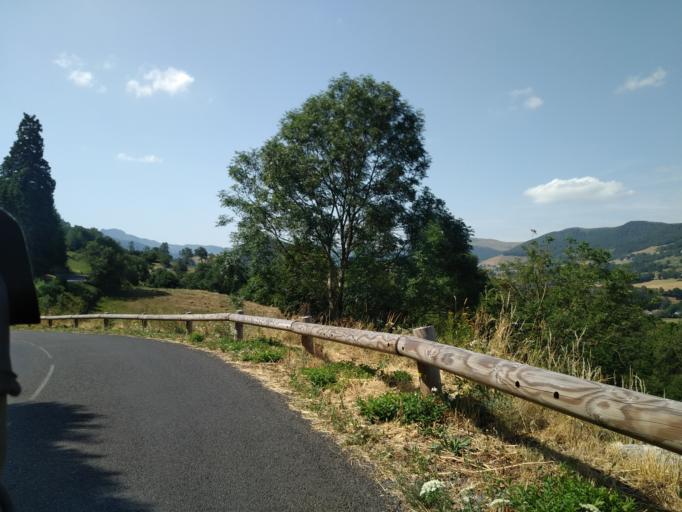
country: FR
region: Auvergne
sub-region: Departement du Cantal
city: Riom-es-Montagnes
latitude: 45.1984
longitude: 2.7172
